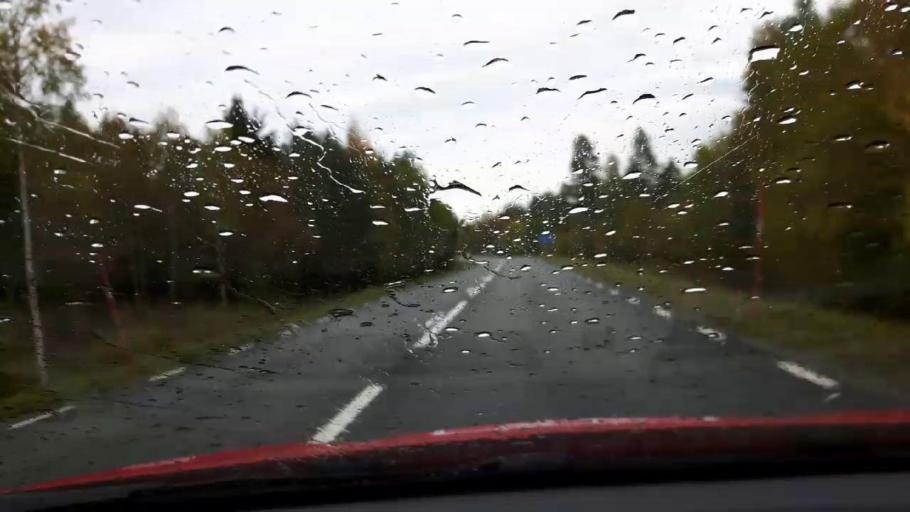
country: SE
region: Jaemtland
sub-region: Krokoms Kommun
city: Krokom
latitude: 63.1216
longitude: 14.2939
